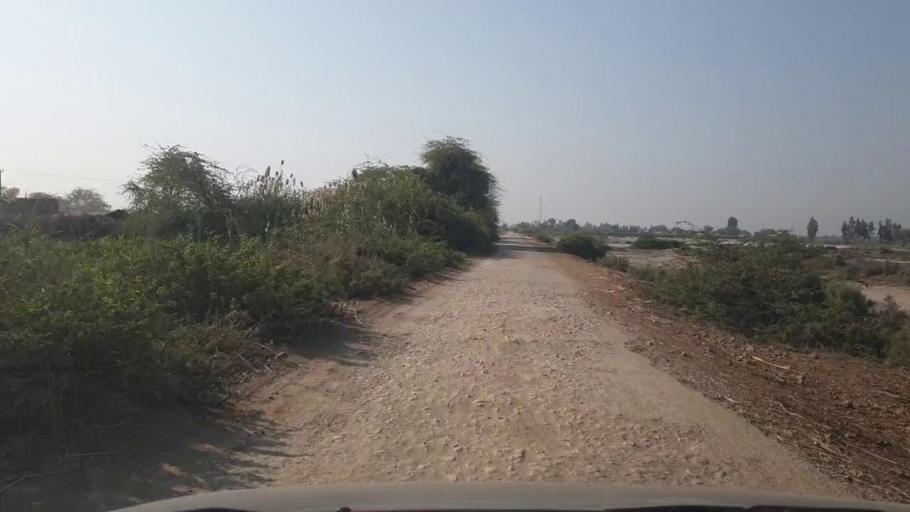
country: PK
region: Sindh
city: Mirwah Gorchani
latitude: 25.3060
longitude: 69.1502
